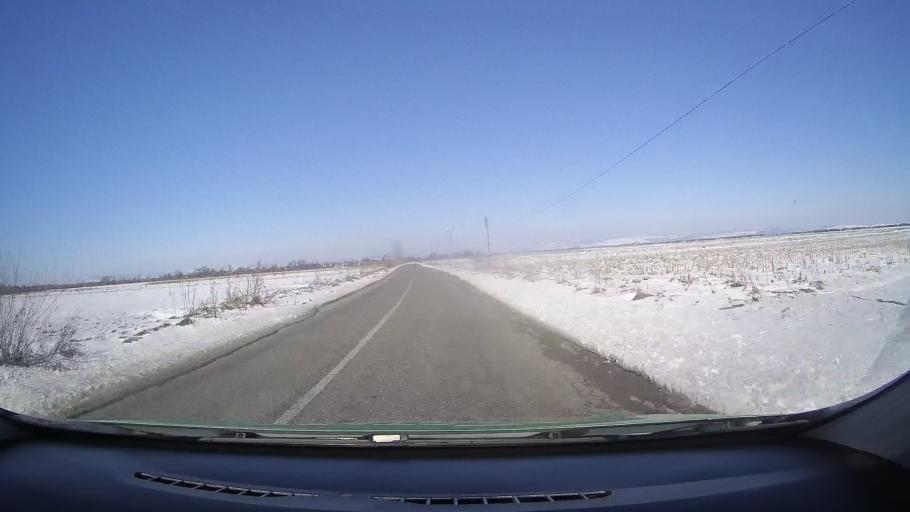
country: RO
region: Brasov
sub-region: Comuna Harseni
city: Harseni
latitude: 45.7439
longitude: 25.0185
